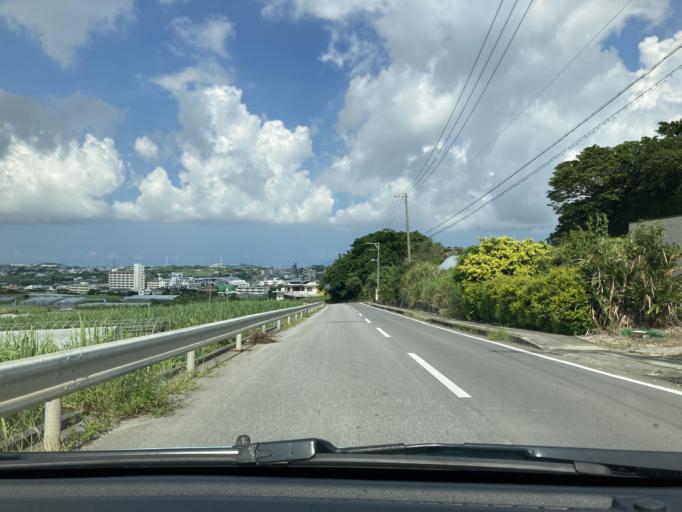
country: JP
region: Okinawa
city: Tomigusuku
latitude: 26.1490
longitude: 127.7587
